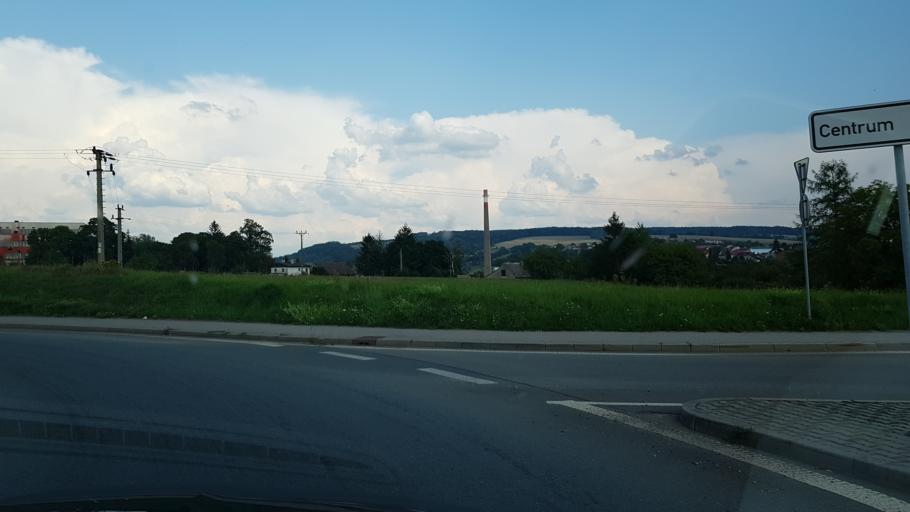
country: CZ
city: Vamberk
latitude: 50.1211
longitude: 16.2838
